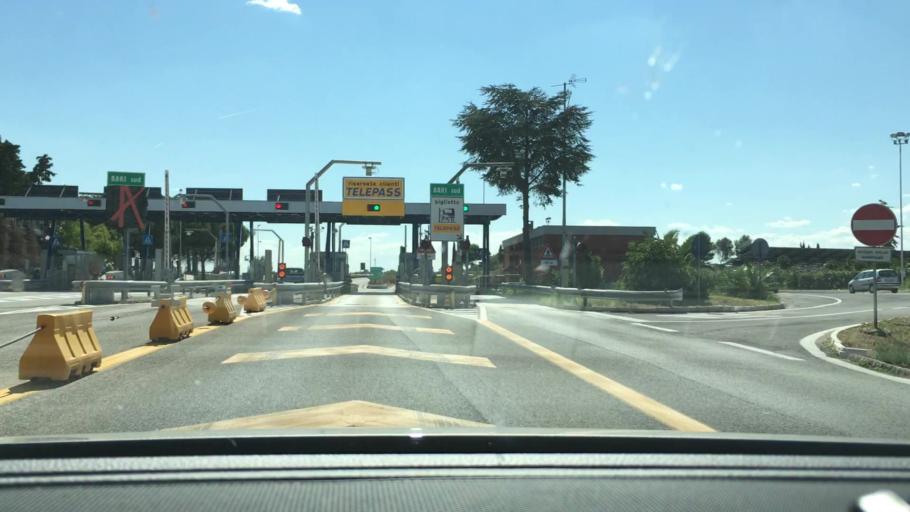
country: IT
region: Apulia
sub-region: Provincia di Bari
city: Bitritto
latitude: 41.0689
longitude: 16.8313
